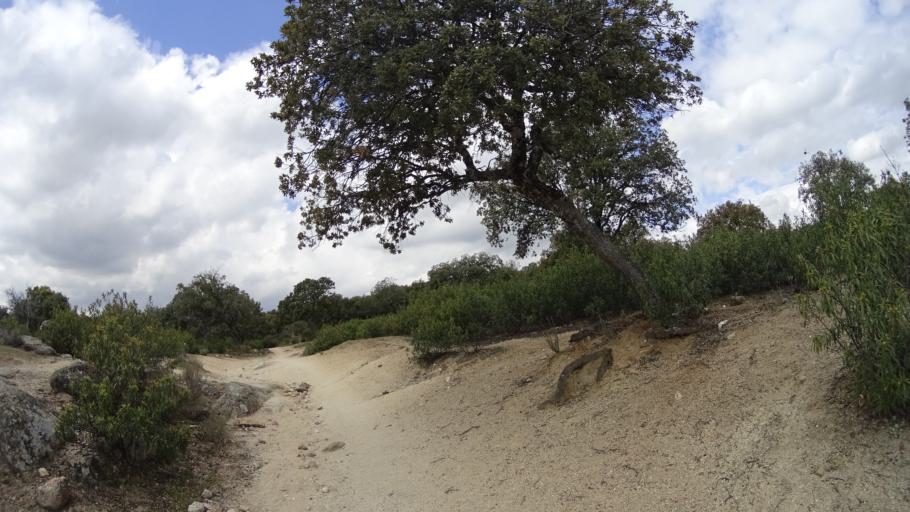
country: ES
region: Madrid
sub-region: Provincia de Madrid
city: Hoyo de Manzanares
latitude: 40.6211
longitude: -3.8867
